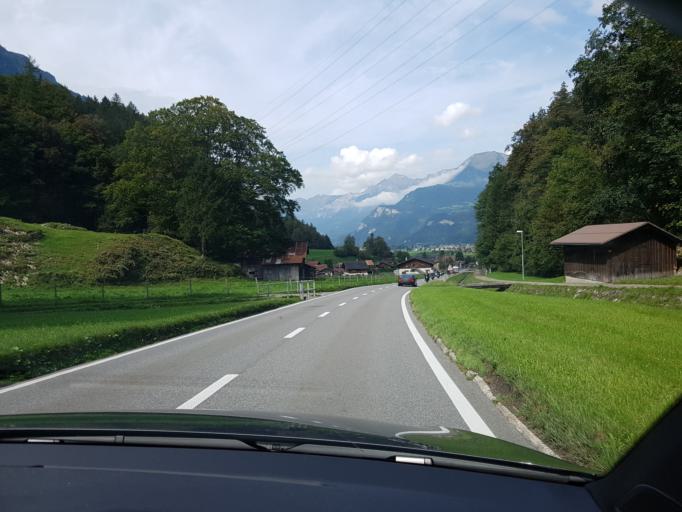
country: CH
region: Bern
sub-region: Interlaken-Oberhasli District
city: Meiringen
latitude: 46.7156
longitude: 8.1958
